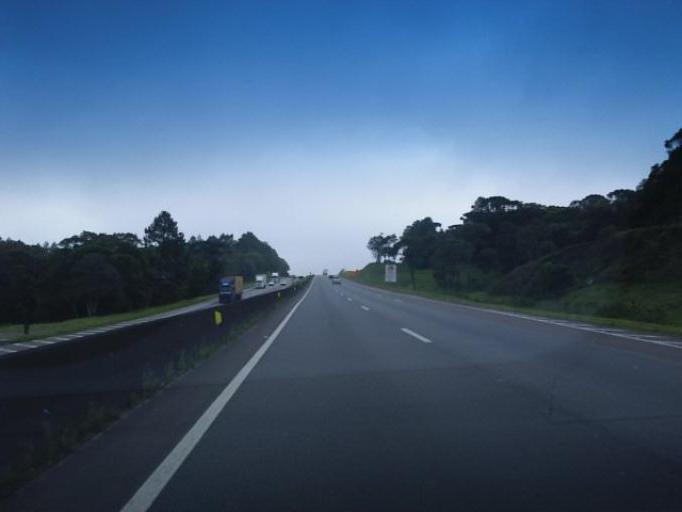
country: BR
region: Parana
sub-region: Sao Jose Dos Pinhais
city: Sao Jose dos Pinhais
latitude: -25.8101
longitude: -49.1337
